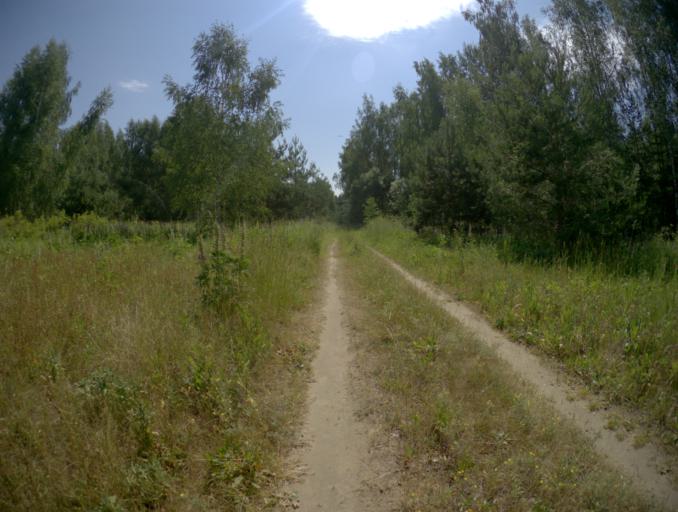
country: RU
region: Vladimir
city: Raduzhnyy
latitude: 56.0213
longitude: 40.2492
